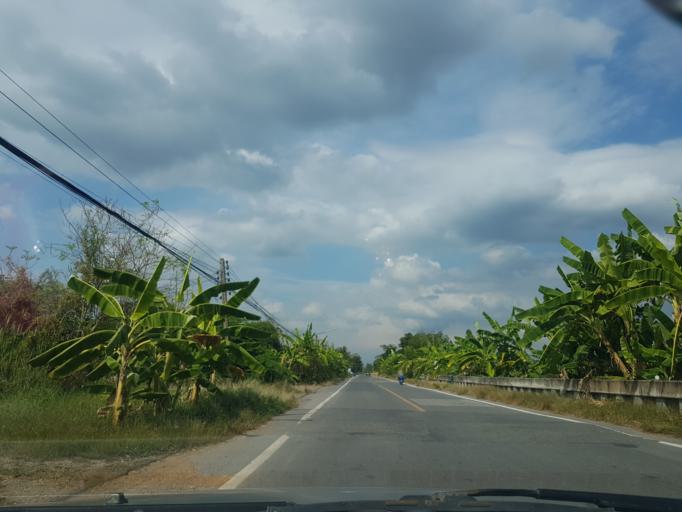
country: TH
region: Pathum Thani
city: Nong Suea
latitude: 14.1575
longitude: 100.8915
